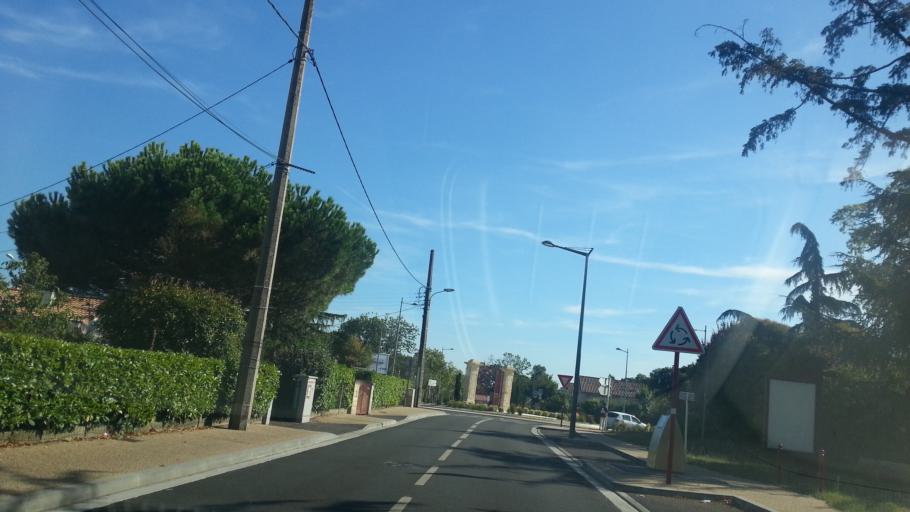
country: FR
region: Aquitaine
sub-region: Departement de la Gironde
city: Bassens
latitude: 44.8965
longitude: -0.5164
